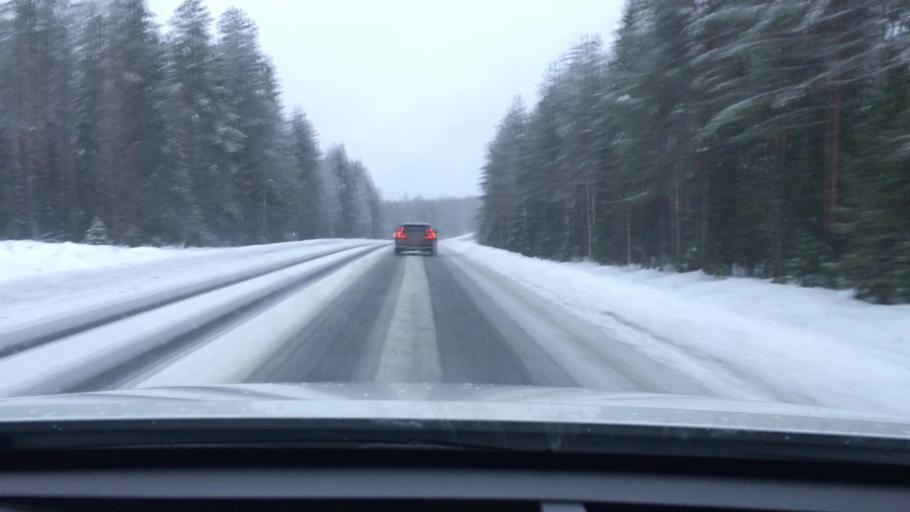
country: FI
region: Northern Savo
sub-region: Ylae-Savo
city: Sonkajaervi
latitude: 63.7720
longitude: 27.4150
